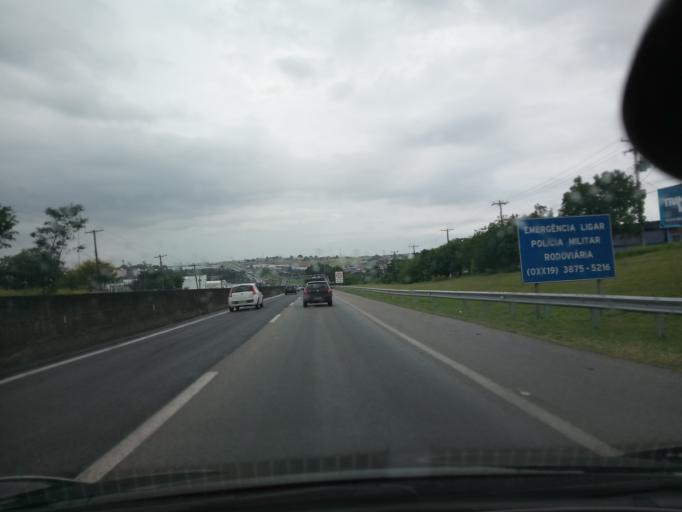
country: BR
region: Sao Paulo
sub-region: Campinas
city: Campinas
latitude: -22.9598
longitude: -47.0965
